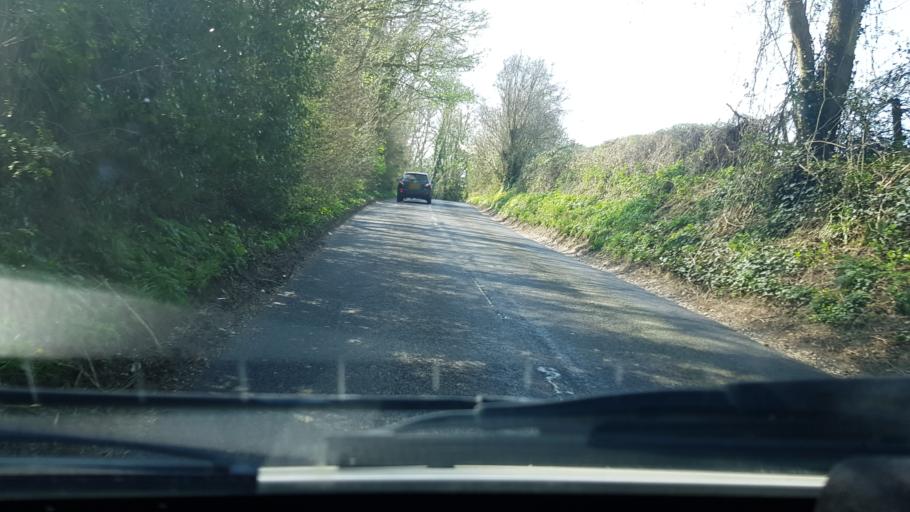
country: GB
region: England
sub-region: West Sussex
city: Chichester
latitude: 50.8664
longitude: -0.7804
